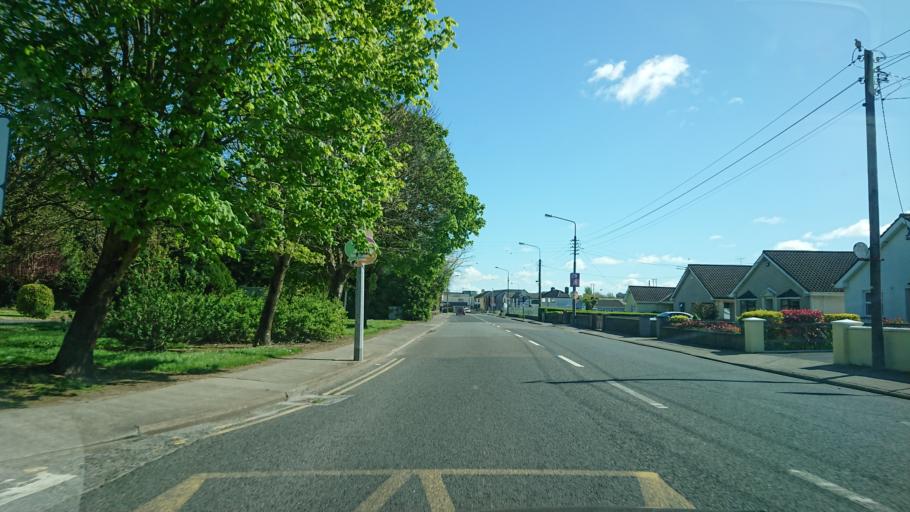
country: IE
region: Munster
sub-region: Waterford
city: Waterford
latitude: 52.2504
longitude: -7.1193
